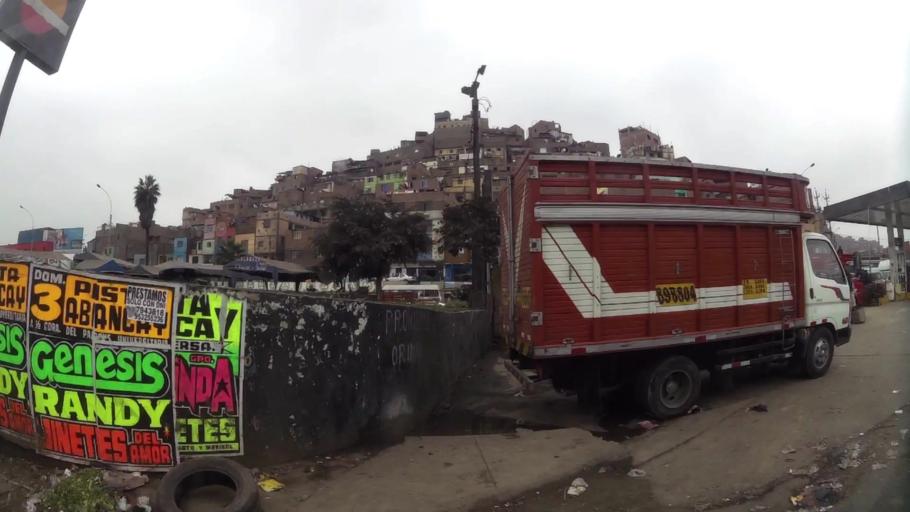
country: PE
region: Lima
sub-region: Lima
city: San Luis
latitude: -12.0607
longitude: -77.0067
